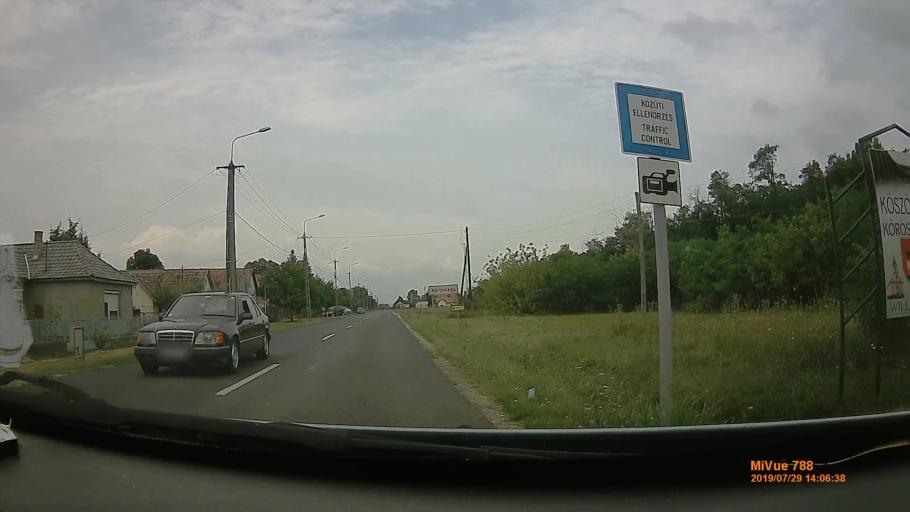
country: HU
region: Somogy
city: Balatonfoldvar
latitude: 46.8187
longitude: 17.9068
